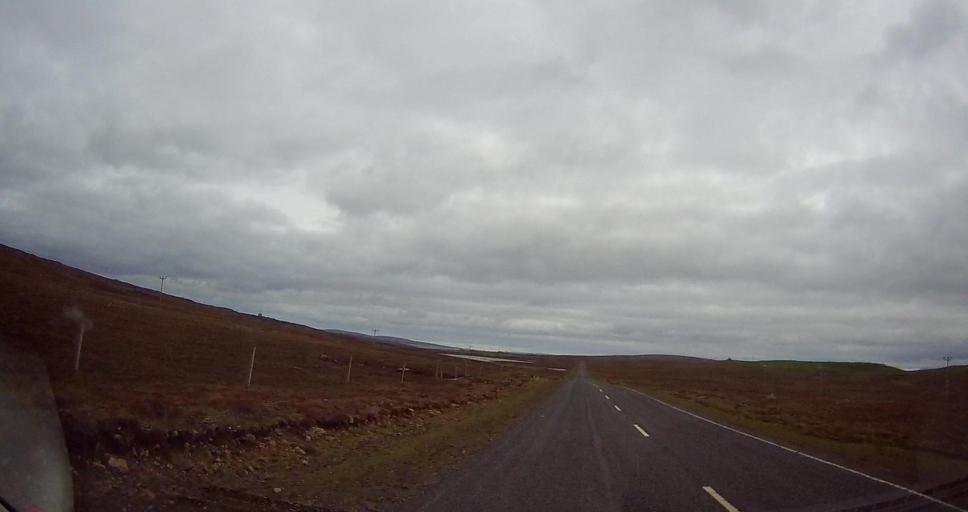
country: GB
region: Scotland
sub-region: Shetland Islands
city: Shetland
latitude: 60.7200
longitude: -0.9109
